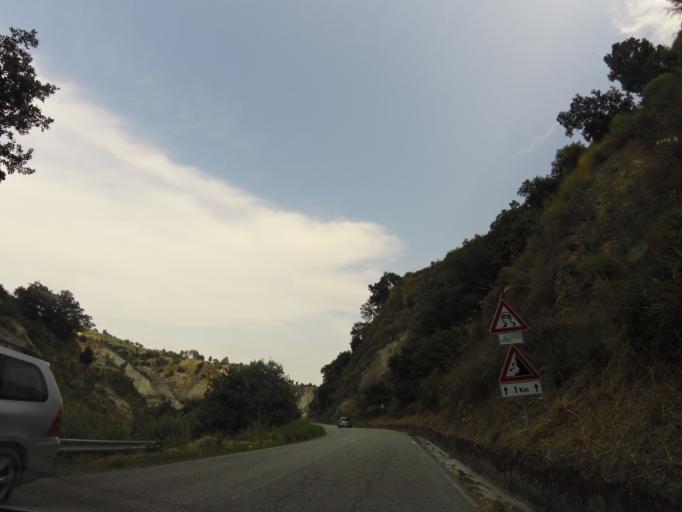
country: IT
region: Calabria
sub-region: Provincia di Reggio Calabria
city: Stilo
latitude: 38.4707
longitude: 16.4829
